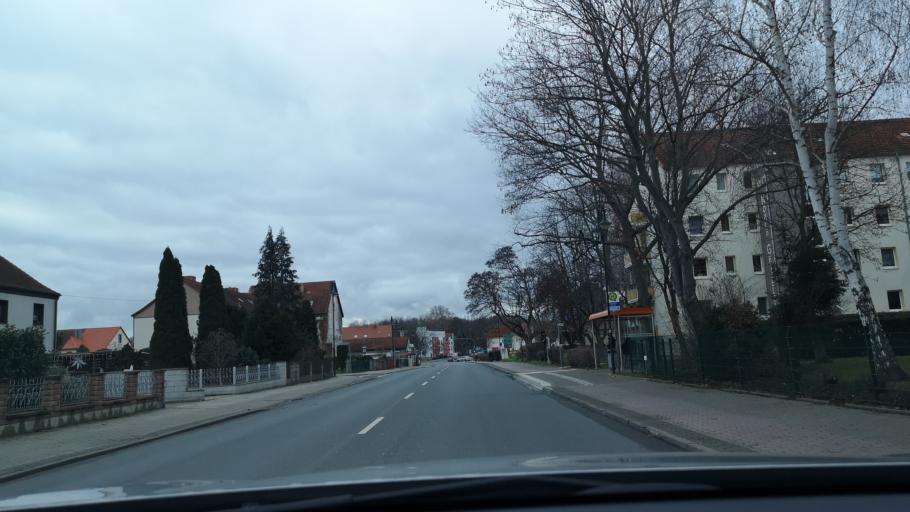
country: DE
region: Saxony-Anhalt
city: Braunsbedra
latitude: 51.2850
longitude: 11.8883
